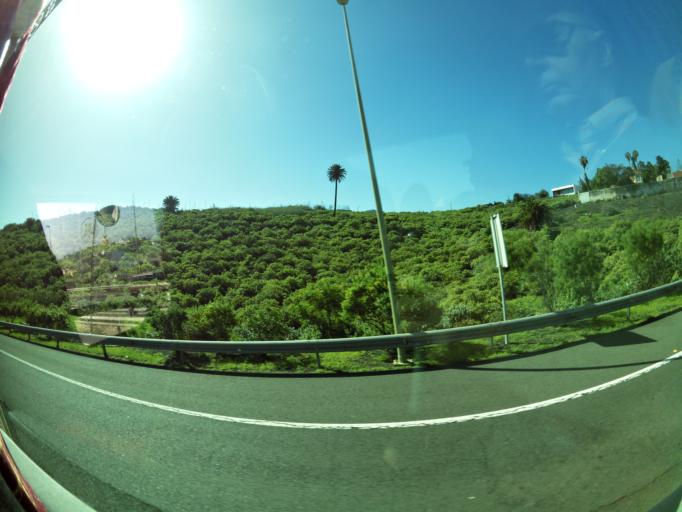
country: ES
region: Canary Islands
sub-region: Provincia de Las Palmas
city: Santa Brigida
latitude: 28.0497
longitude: -15.4550
